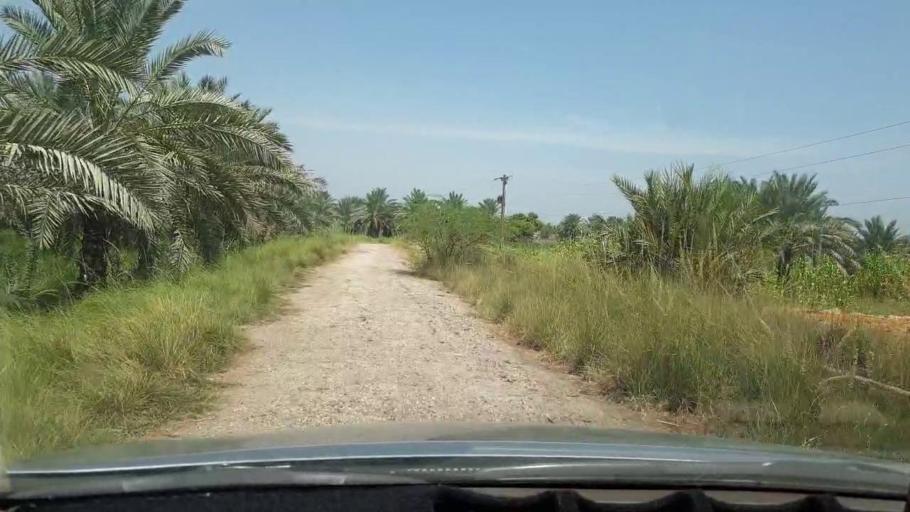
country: PK
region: Sindh
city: Khairpur
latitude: 27.4917
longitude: 68.7693
